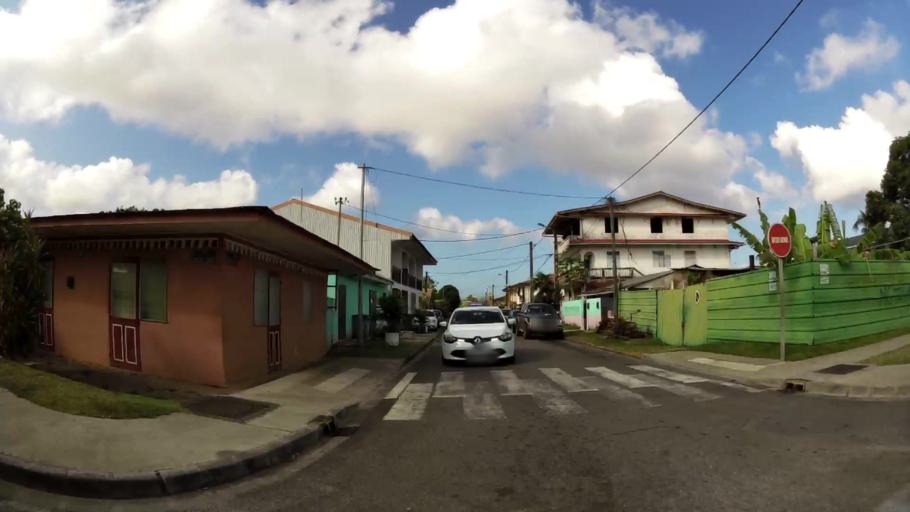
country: GF
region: Guyane
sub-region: Guyane
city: Cayenne
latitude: 4.9341
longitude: -52.3204
